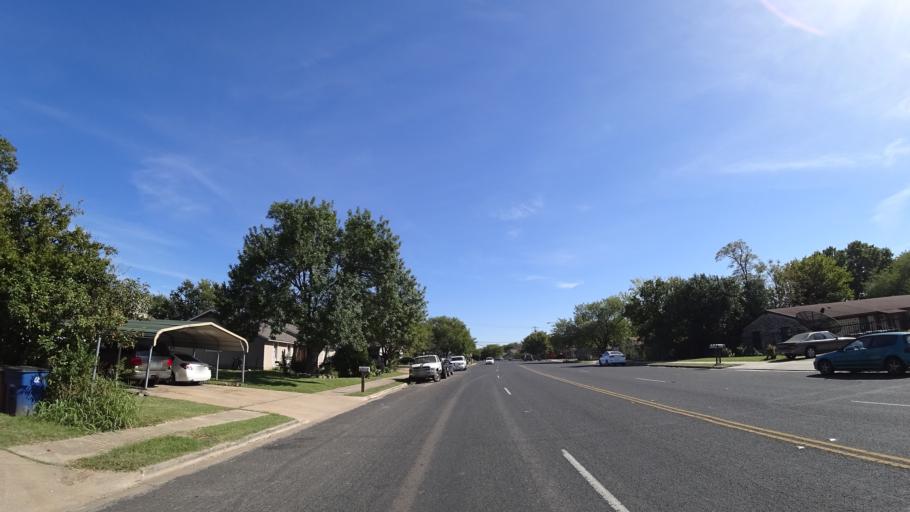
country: US
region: Texas
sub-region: Travis County
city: Austin
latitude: 30.1993
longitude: -97.7477
